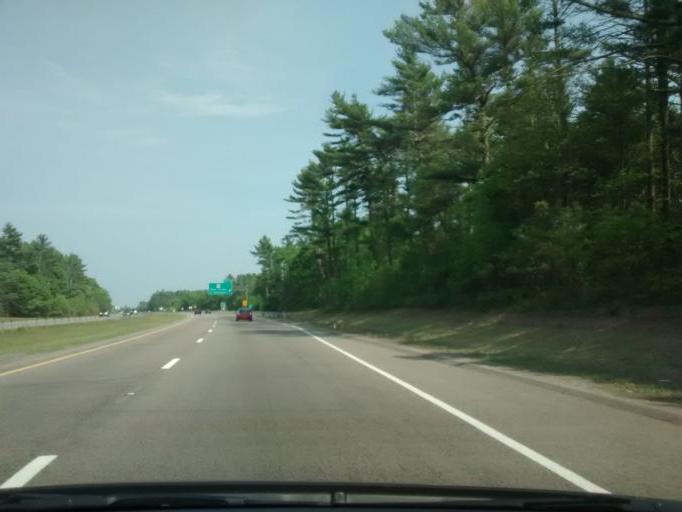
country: US
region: Massachusetts
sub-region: Plymouth County
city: Middleborough Center
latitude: 41.8477
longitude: -70.8555
